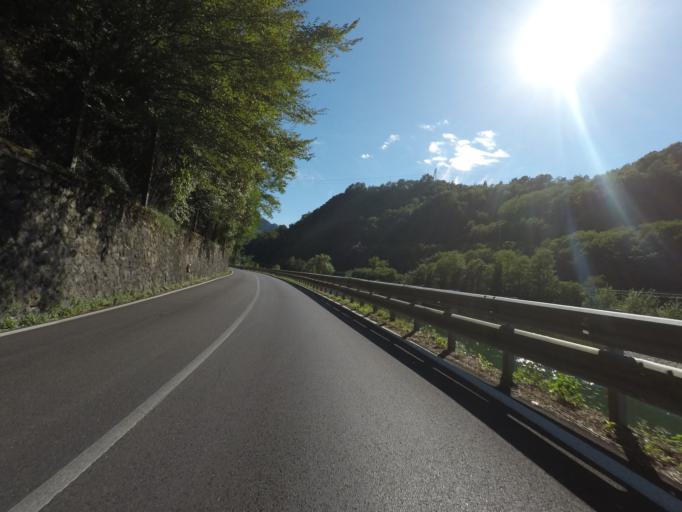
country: IT
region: Tuscany
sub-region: Provincia di Lucca
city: Bagni di Lucca
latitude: 43.9929
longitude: 10.5539
